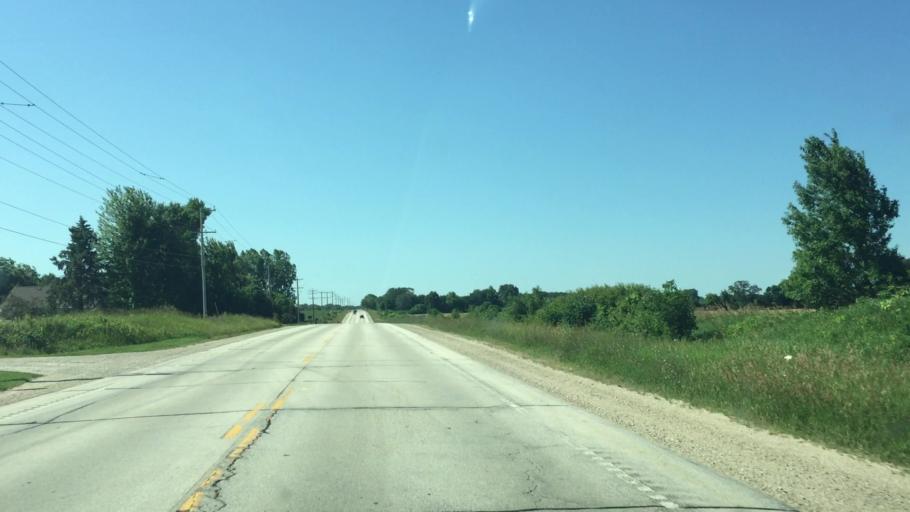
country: US
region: Wisconsin
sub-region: Calumet County
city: Sherwood
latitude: 44.1512
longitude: -88.2648
